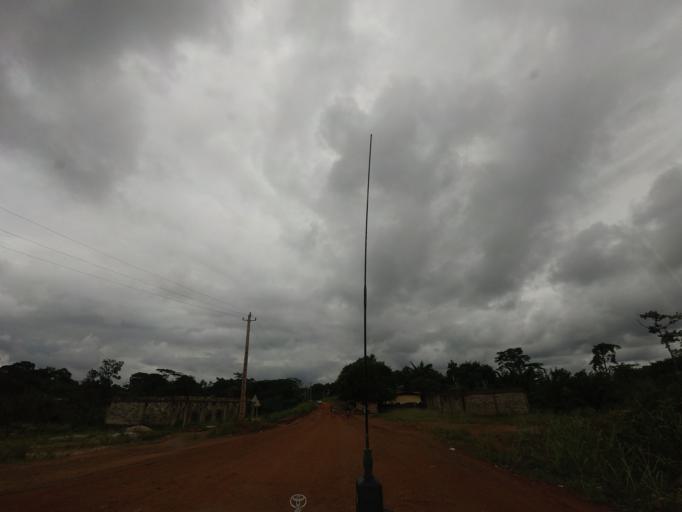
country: LR
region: Nimba
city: Sanniquellie
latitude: 7.3431
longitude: -8.9630
